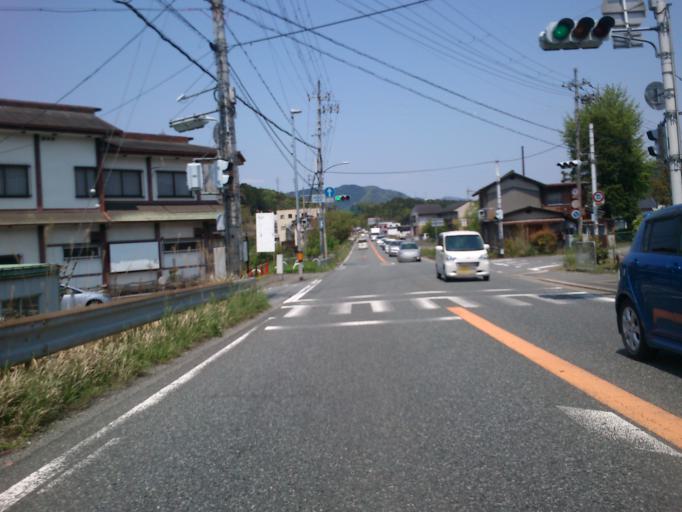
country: JP
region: Kyoto
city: Fukuchiyama
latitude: 35.3063
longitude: 135.1034
